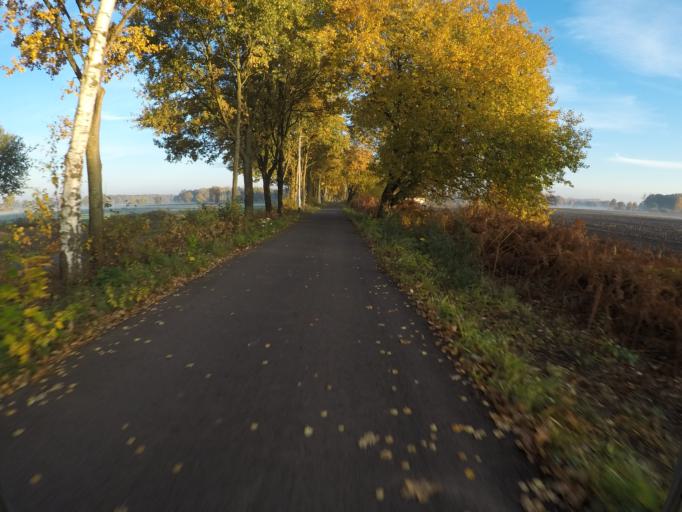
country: BE
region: Flanders
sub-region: Provincie Antwerpen
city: Hulshout
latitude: 51.0995
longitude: 4.8254
